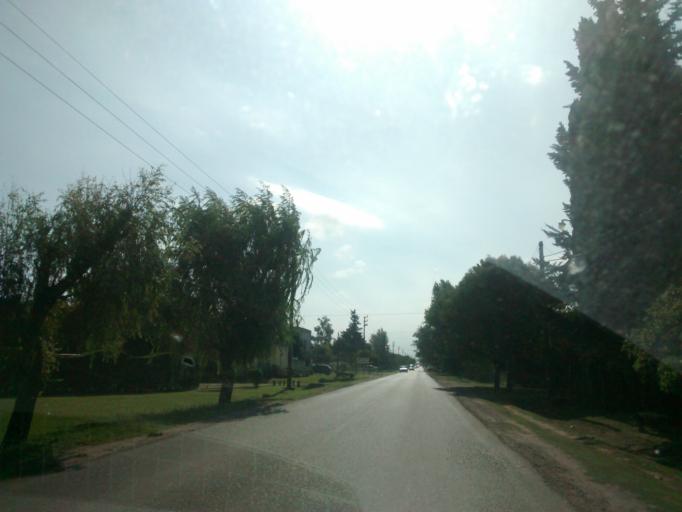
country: AR
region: Buenos Aires
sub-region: Partido de La Plata
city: La Plata
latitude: -34.9753
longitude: -57.8692
